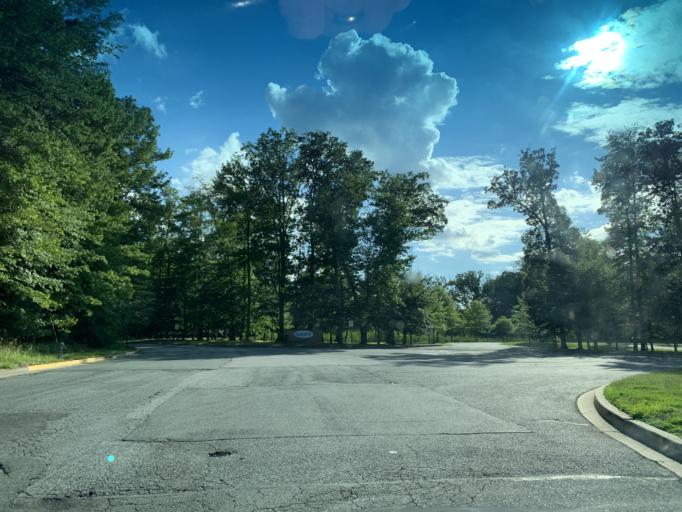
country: US
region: Maryland
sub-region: Harford County
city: Havre de Grace
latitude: 39.5305
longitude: -76.1159
